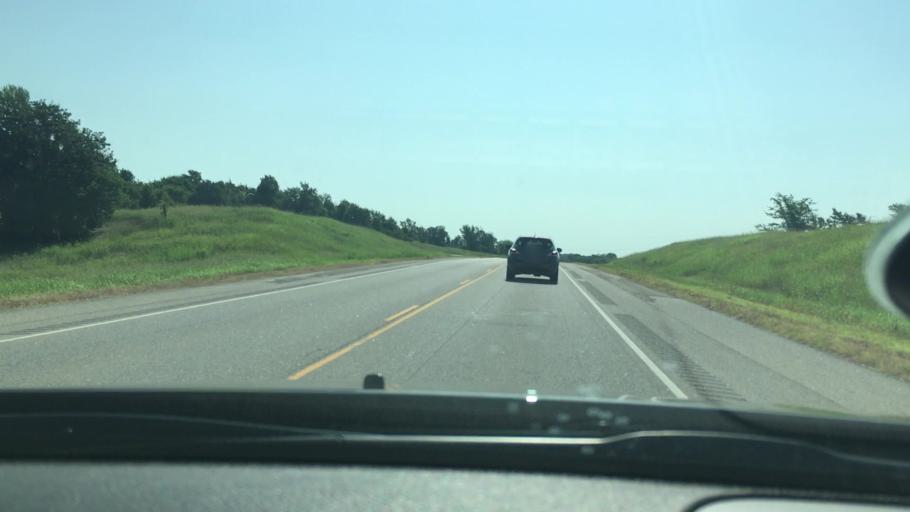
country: US
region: Oklahoma
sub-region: Pontotoc County
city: Ada
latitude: 34.6424
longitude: -96.4975
